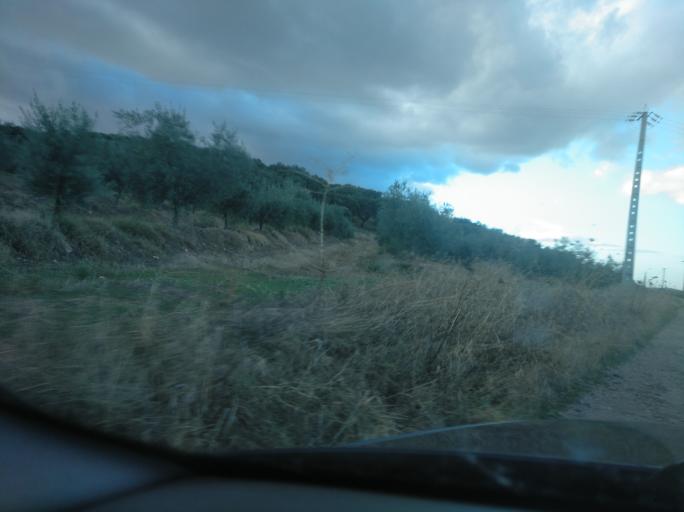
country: PT
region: Portalegre
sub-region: Campo Maior
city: Campo Maior
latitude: 39.0461
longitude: -6.9958
